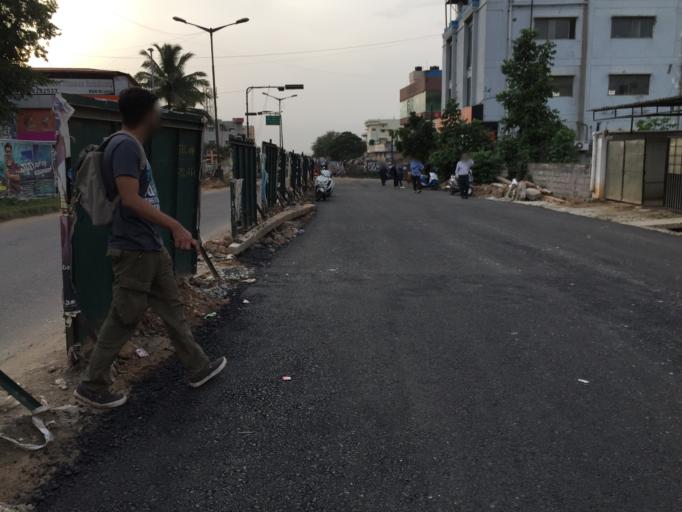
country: IN
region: Karnataka
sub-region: Bangalore Urban
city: Bangalore
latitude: 12.9302
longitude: 77.5439
